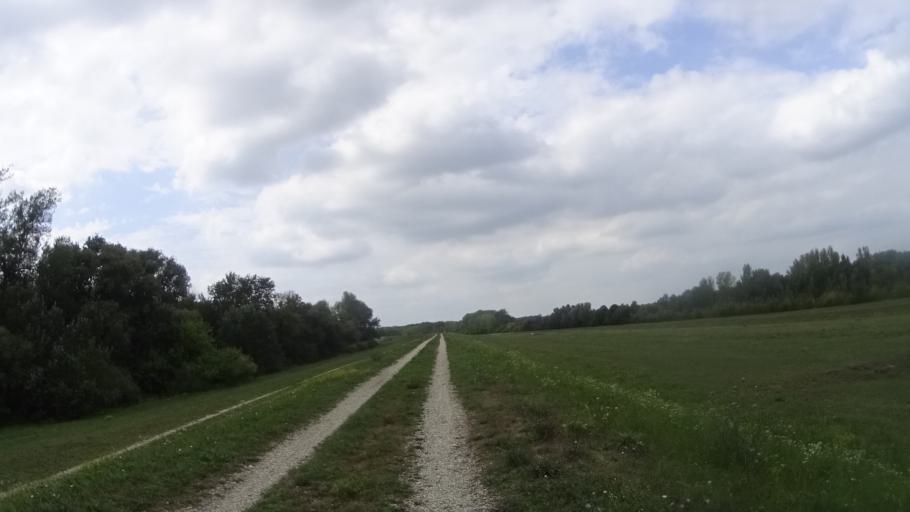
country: SK
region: Trnavsky
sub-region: Okres Dunajska Streda
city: Velky Meder
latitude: 47.7543
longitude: 17.7620
